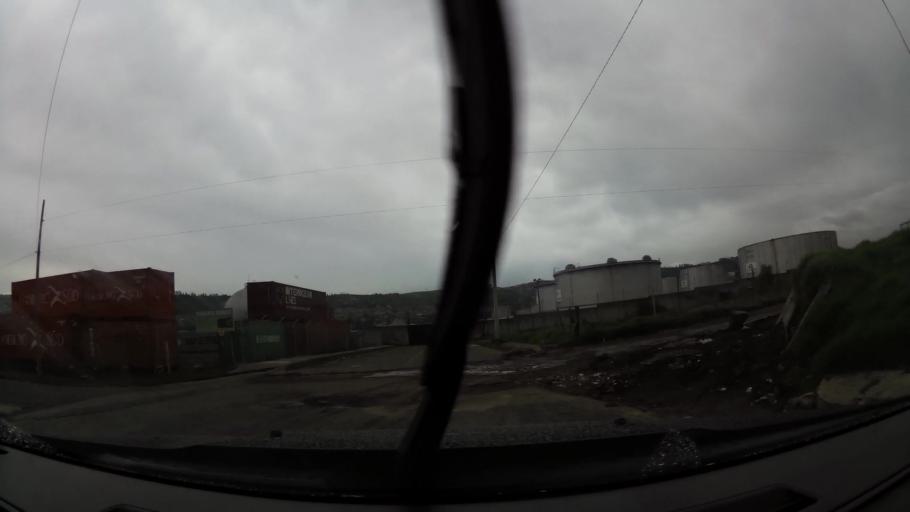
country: EC
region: Pichincha
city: Sangolqui
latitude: -0.3217
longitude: -78.5429
